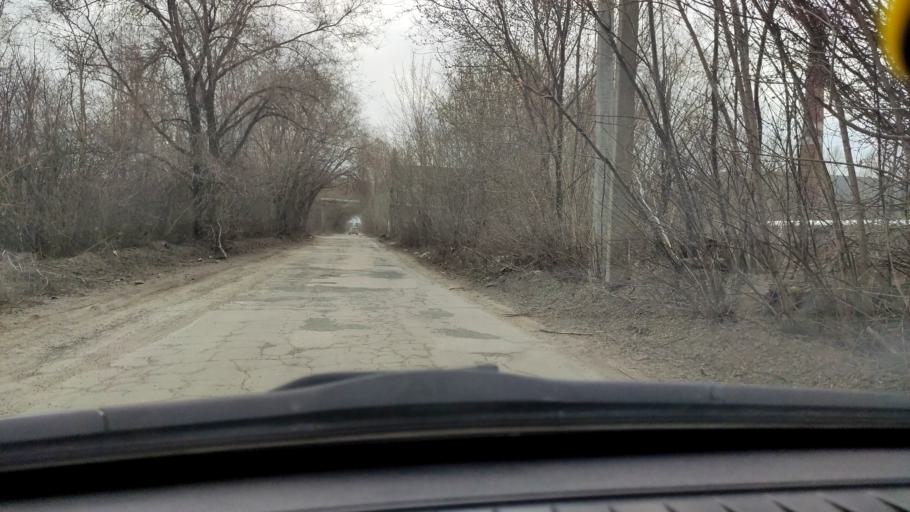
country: RU
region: Samara
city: Tol'yatti
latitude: 53.5210
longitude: 49.4545
